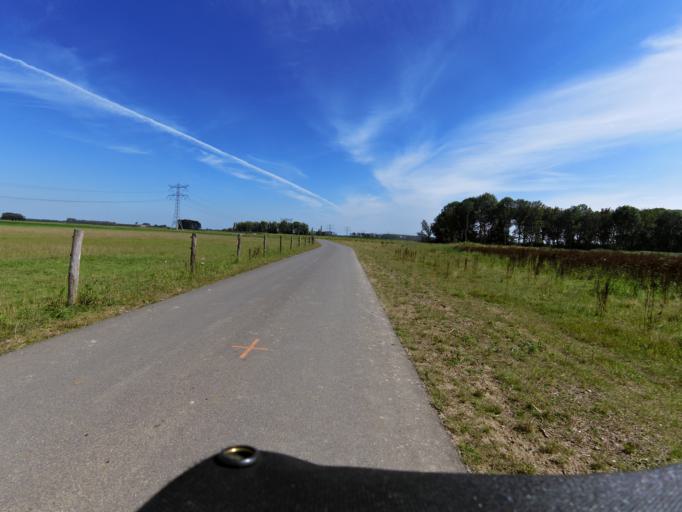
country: NL
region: South Holland
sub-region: Gemeente Hardinxveld-Giessendam
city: Neder-Hardinxveld
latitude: 51.7788
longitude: 4.8207
